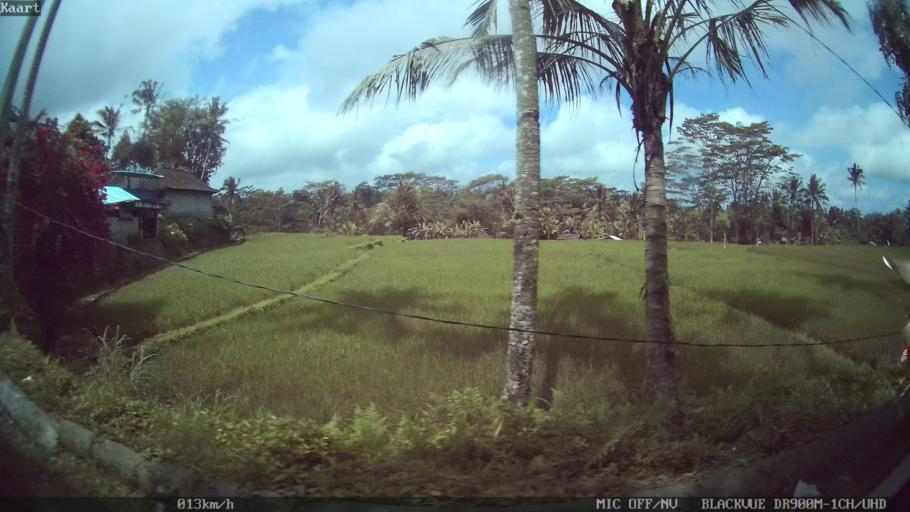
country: ID
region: Bali
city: Banjar Susut Kaja
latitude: -8.4446
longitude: 115.3292
